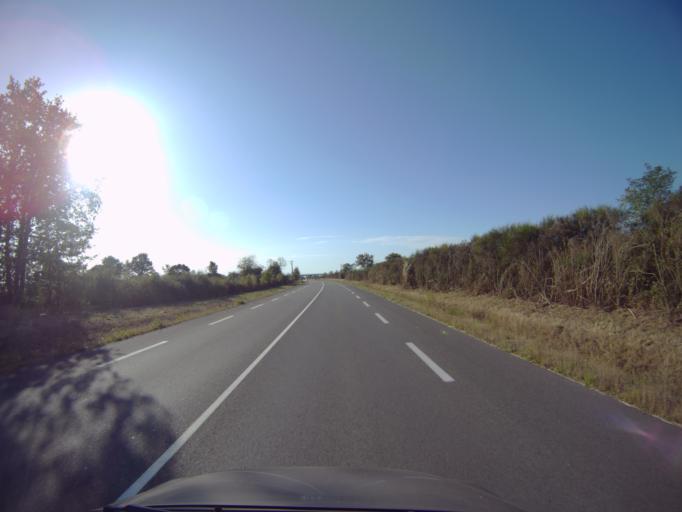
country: FR
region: Pays de la Loire
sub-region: Departement de la Vendee
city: Moutiers-les-Mauxfaits
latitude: 46.4868
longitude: -1.4434
